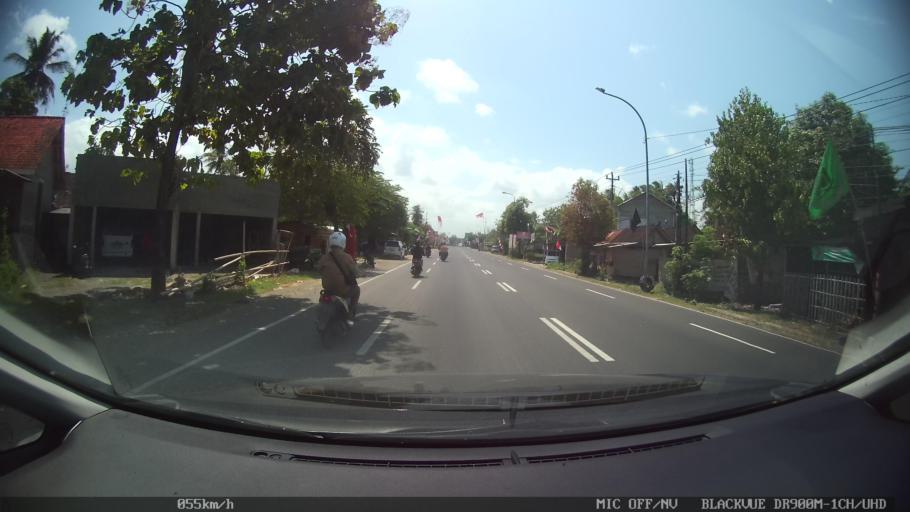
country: ID
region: Daerah Istimewa Yogyakarta
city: Srandakan
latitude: -7.9348
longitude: 110.2612
